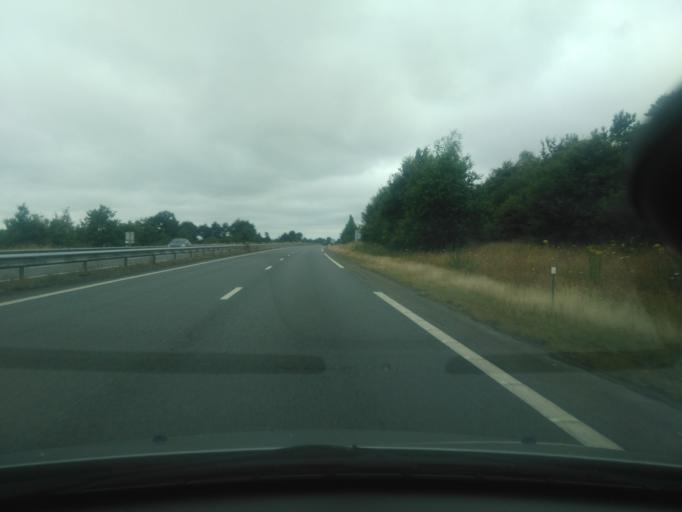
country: FR
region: Brittany
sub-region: Departement des Cotes-d'Armor
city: Jugon-les-Lacs
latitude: 48.4186
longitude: -2.2791
